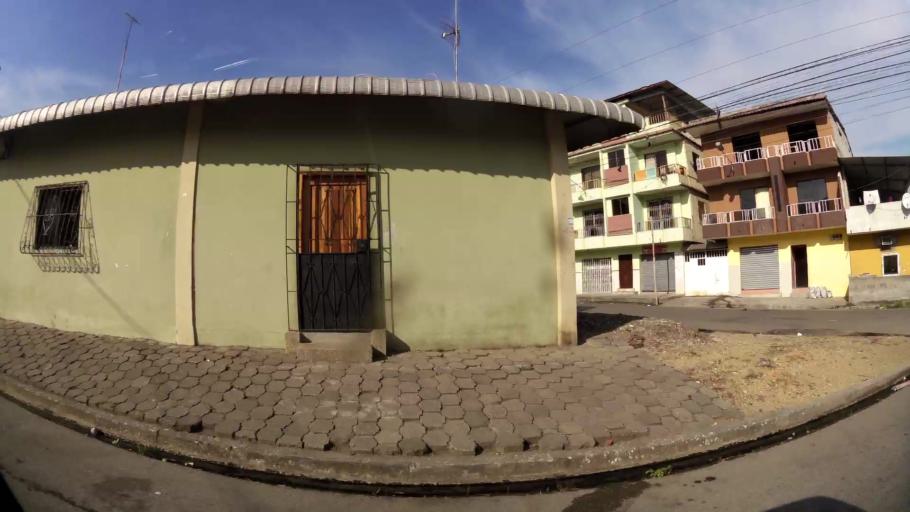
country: EC
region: Guayas
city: Eloy Alfaro
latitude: -2.0762
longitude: -79.9328
